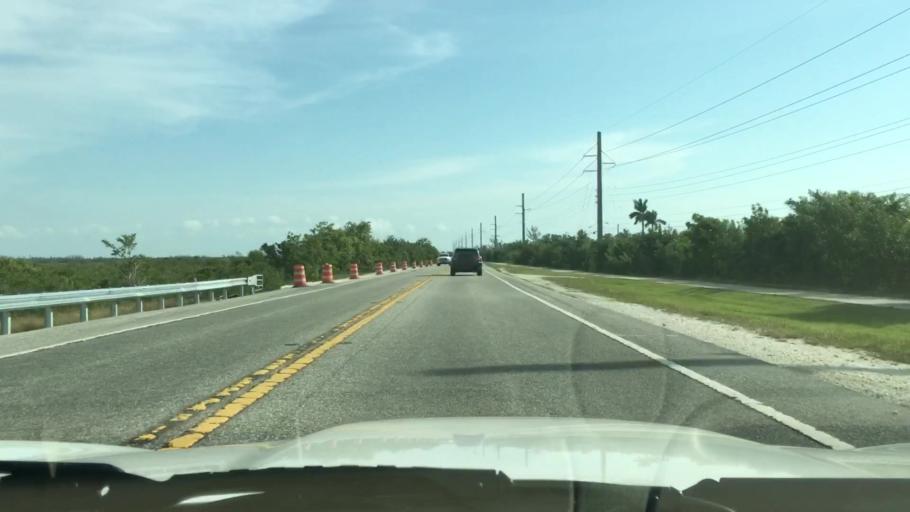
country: US
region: Florida
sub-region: Monroe County
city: Cudjoe Key
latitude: 24.6629
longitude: -81.5128
